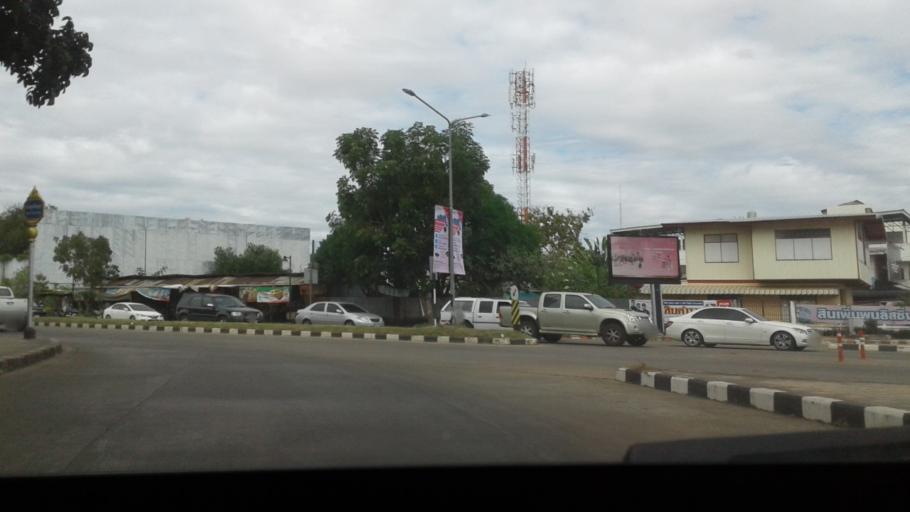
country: TH
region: Changwat Udon Thani
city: Udon Thani
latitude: 17.4186
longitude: 102.7863
